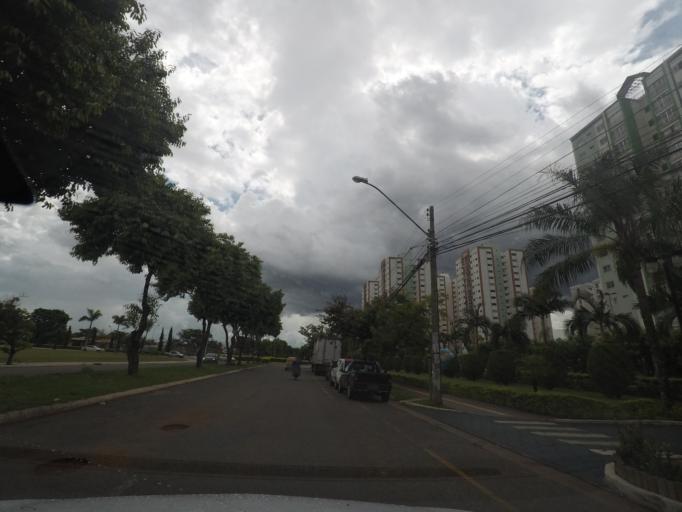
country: BR
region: Goias
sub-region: Goiania
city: Goiania
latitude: -16.7108
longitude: -49.3284
